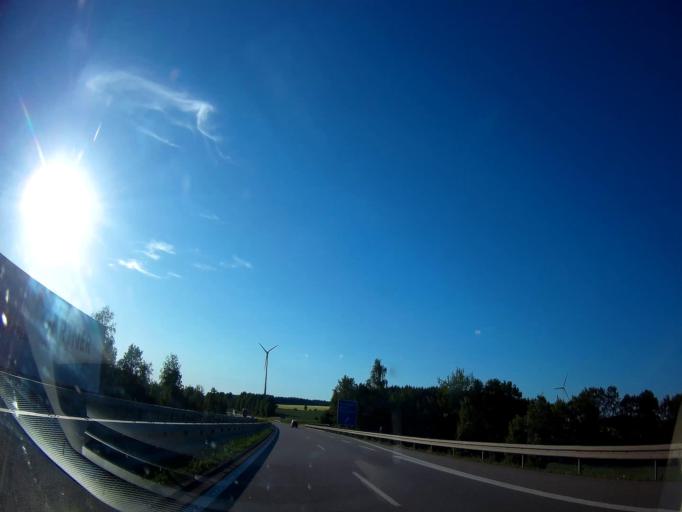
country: DE
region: Bavaria
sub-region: Upper Palatinate
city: Brunn
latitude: 49.1428
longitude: 11.8602
